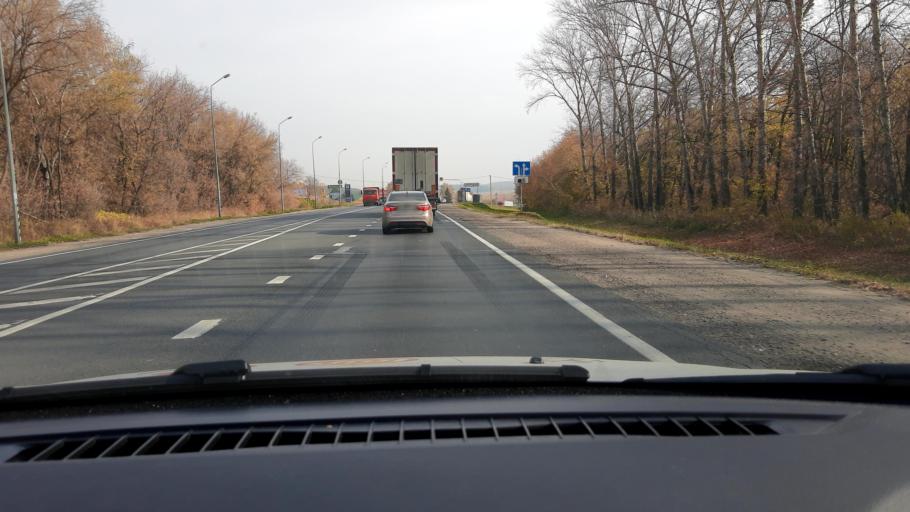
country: RU
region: Nizjnij Novgorod
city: Pamyat' Parizhskoy Kommuny
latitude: 56.0456
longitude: 44.4301
